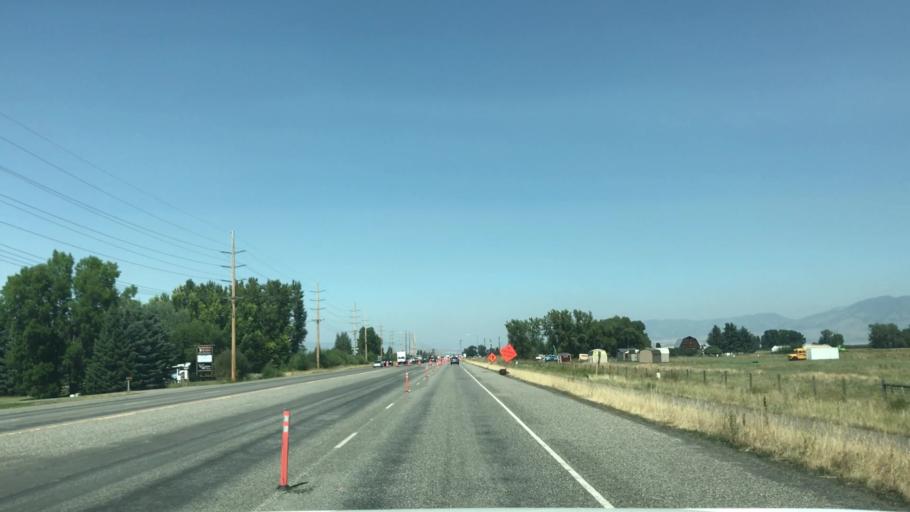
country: US
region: Montana
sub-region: Gallatin County
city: Belgrade
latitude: 45.7115
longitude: -111.1851
